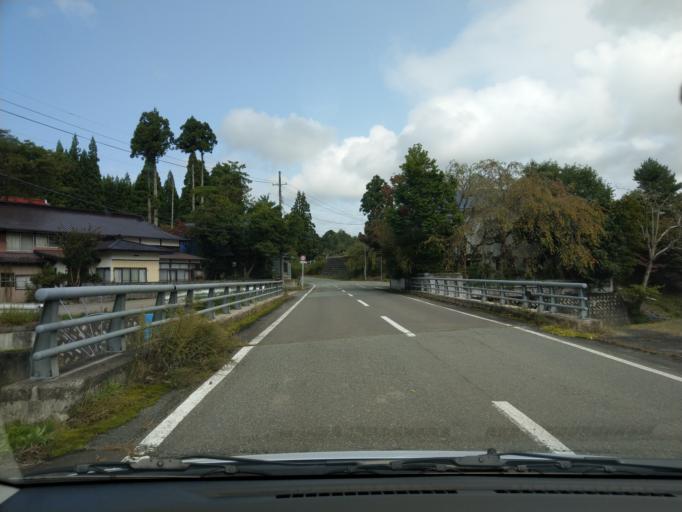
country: JP
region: Akita
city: Omagari
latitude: 39.5060
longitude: 140.3124
